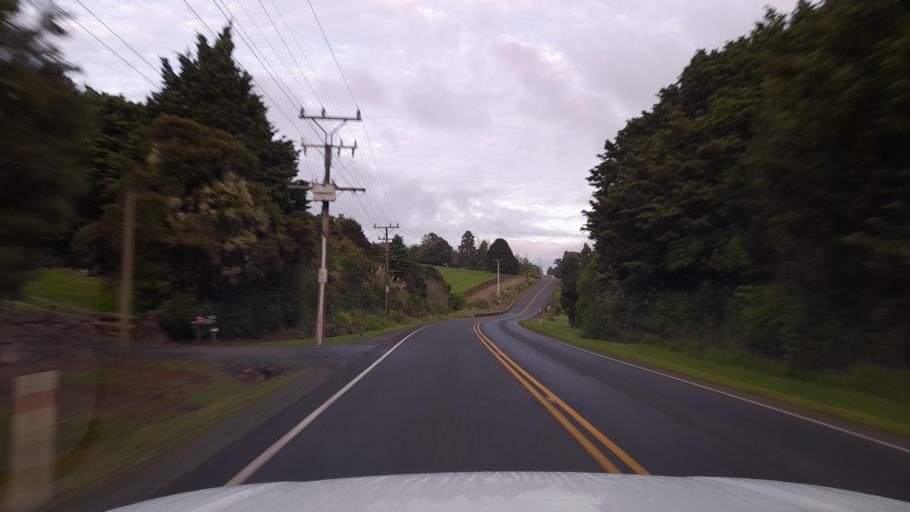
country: NZ
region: Northland
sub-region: Whangarei
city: Maungatapere
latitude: -35.7550
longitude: 174.1763
